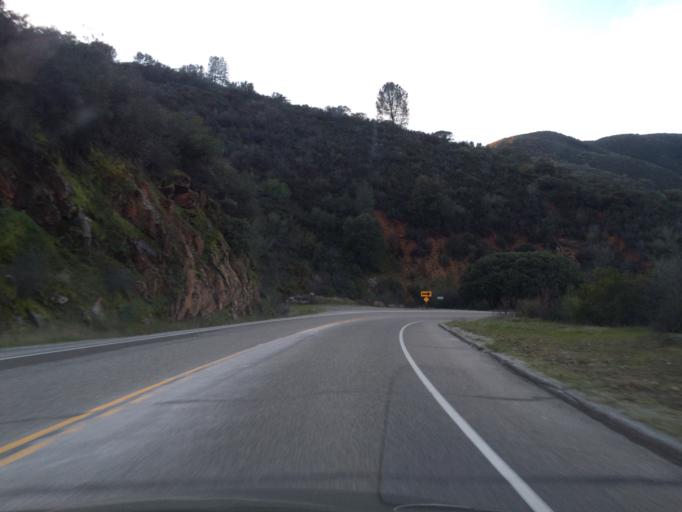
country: US
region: California
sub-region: Mariposa County
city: Midpines
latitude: 37.5859
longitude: -119.9637
